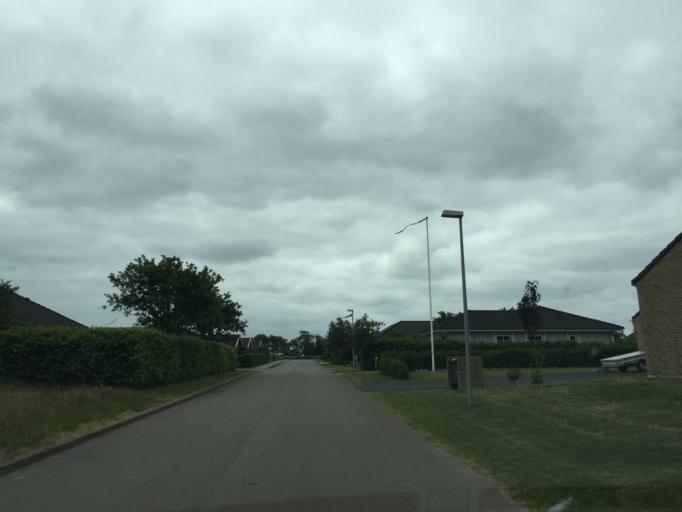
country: DK
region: South Denmark
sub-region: Tonder Kommune
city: Sherrebek
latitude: 55.1529
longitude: 8.7506
